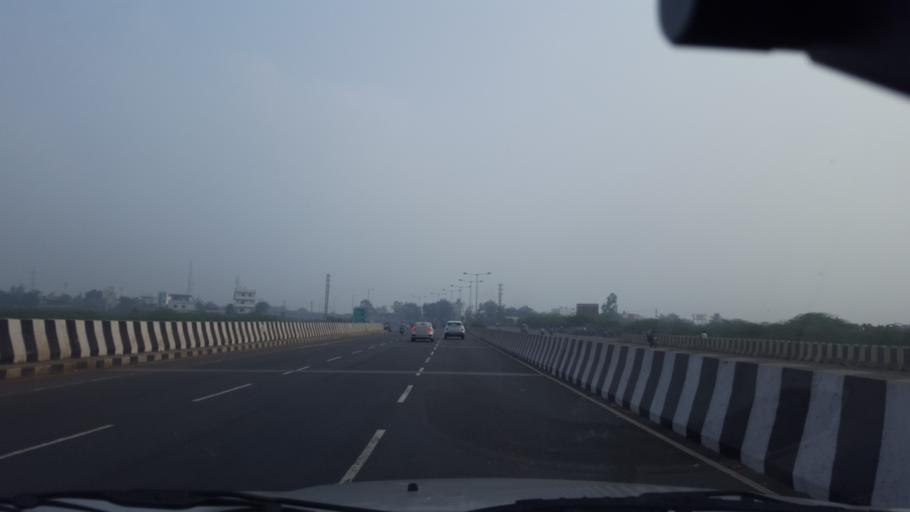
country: IN
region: Andhra Pradesh
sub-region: Prakasam
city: Ongole
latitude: 15.5476
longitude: 80.0547
